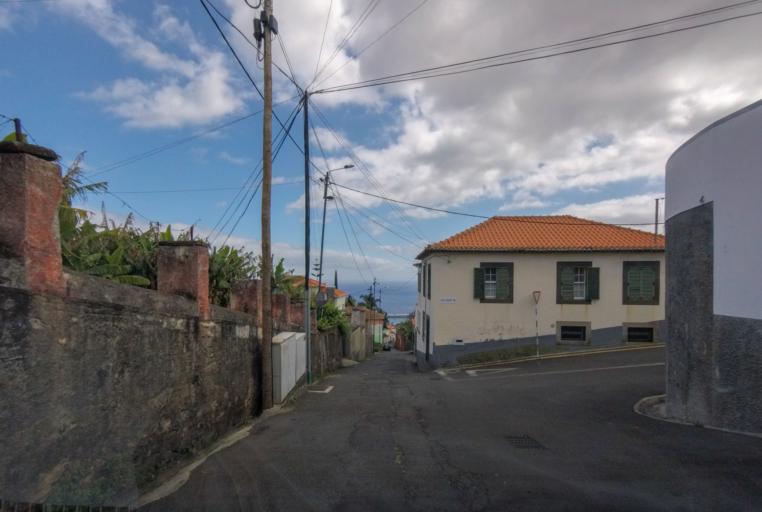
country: PT
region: Madeira
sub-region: Funchal
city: Nossa Senhora do Monte
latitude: 32.6633
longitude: -16.9049
